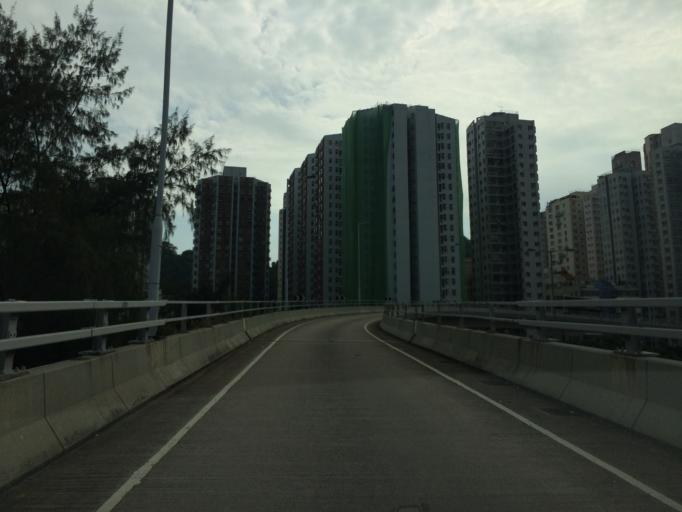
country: HK
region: Wanchai
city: Wan Chai
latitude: 22.2796
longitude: 114.2273
